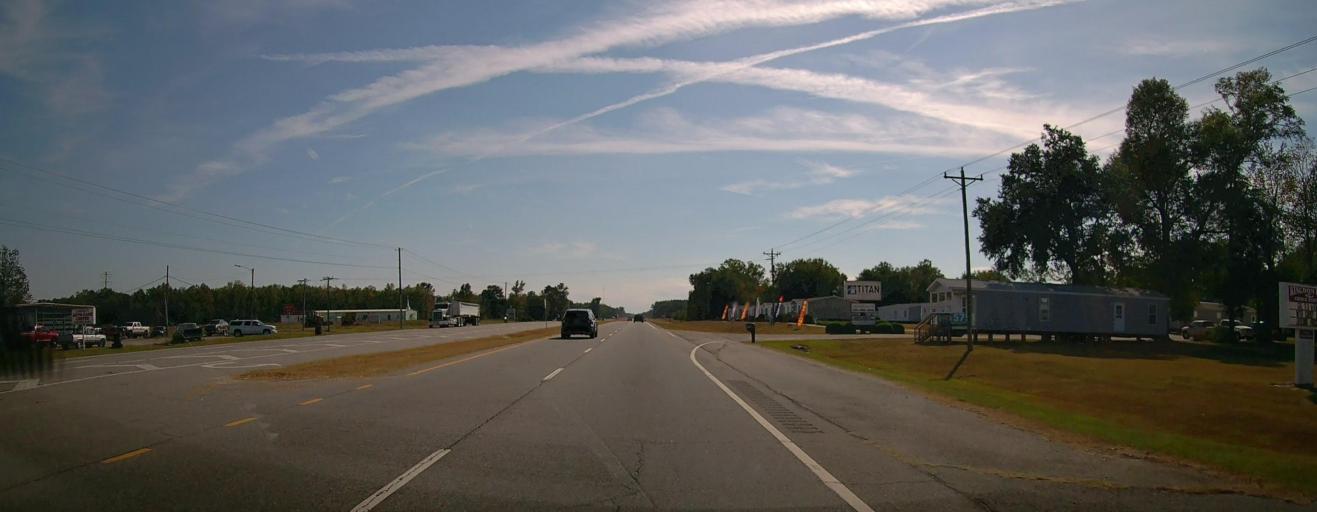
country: US
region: Georgia
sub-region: Dougherty County
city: Putney
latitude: 31.5247
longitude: -84.1157
